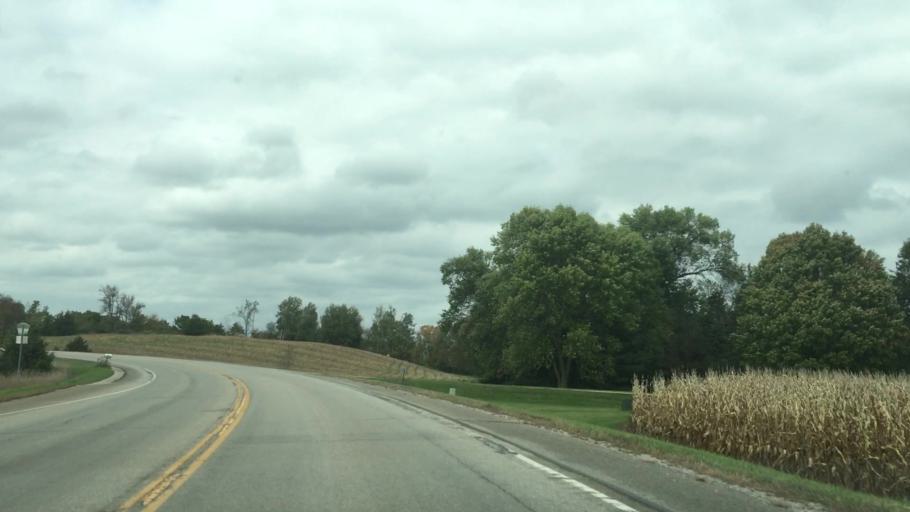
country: US
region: Minnesota
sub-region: Fillmore County
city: Chatfield
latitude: 43.8022
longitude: -92.1289
